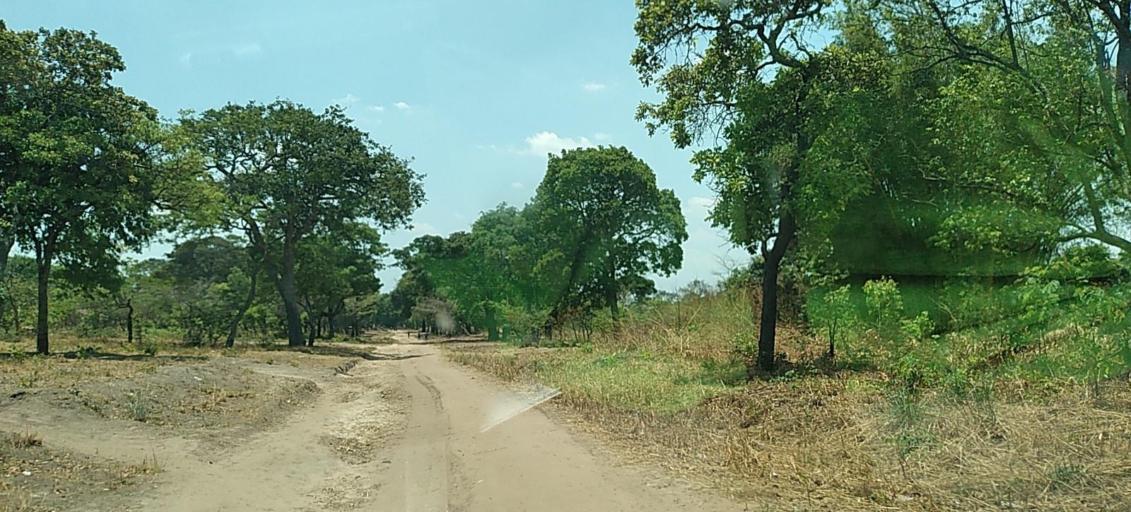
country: CD
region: Katanga
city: Kolwezi
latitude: -11.3766
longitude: 25.2163
